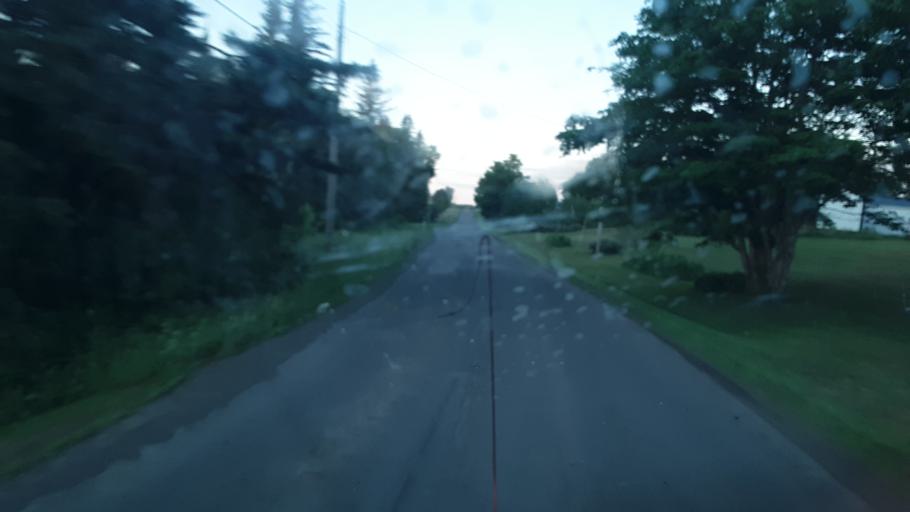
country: US
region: Maine
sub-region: Aroostook County
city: Caribou
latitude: 46.8671
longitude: -68.1375
